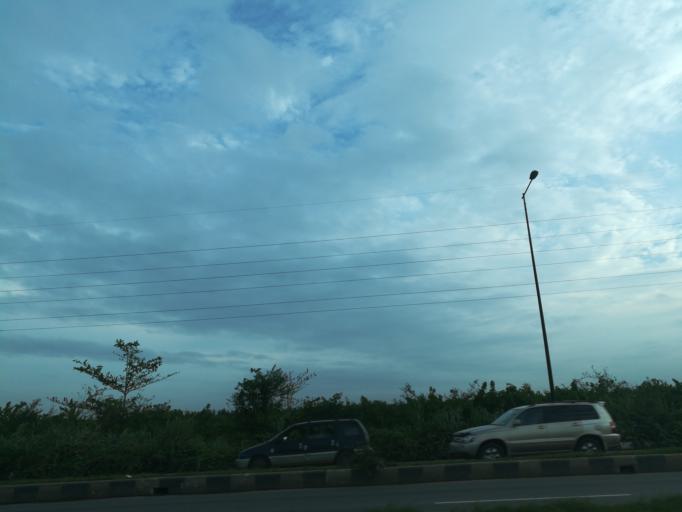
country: NG
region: Lagos
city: Ebute Ikorodu
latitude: 6.6215
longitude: 3.4531
